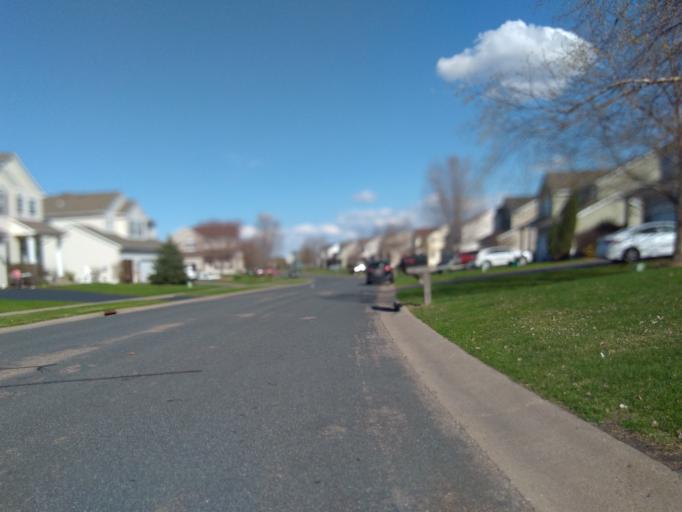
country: US
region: Minnesota
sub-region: Dakota County
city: Rosemount
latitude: 44.7401
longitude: -93.1045
